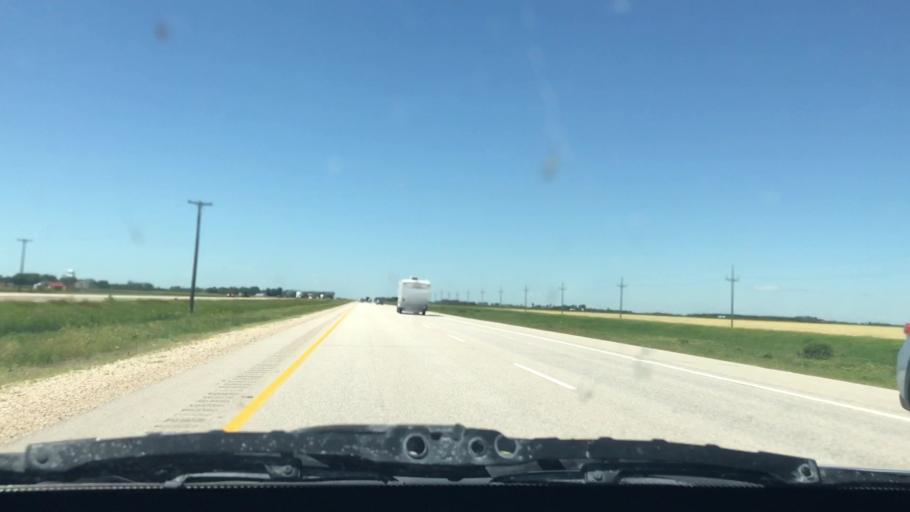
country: CA
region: Manitoba
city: Steinbach
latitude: 49.7226
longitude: -96.6997
